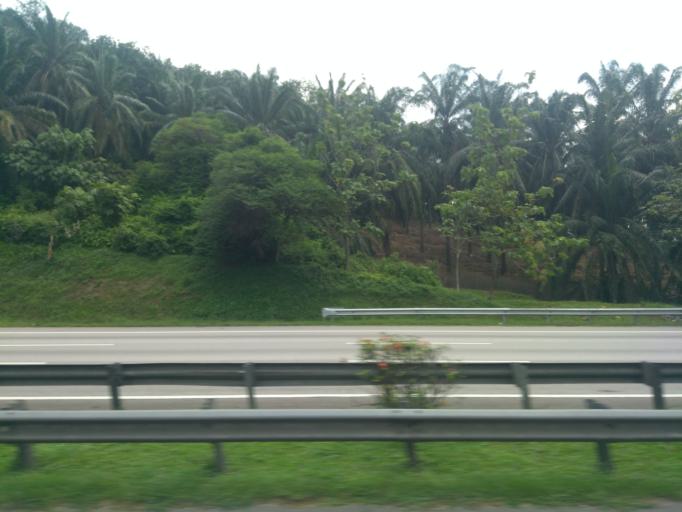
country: MY
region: Negeri Sembilan
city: Seremban
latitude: 2.6430
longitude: 101.9939
